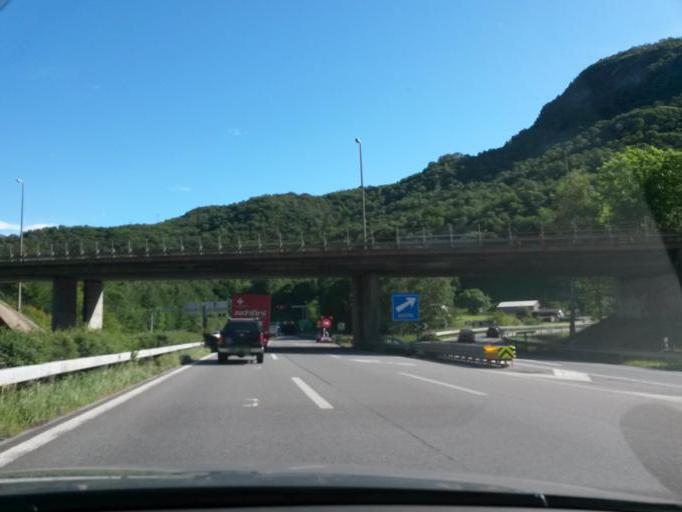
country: CH
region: Ticino
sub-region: Bellinzona District
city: Cadenazzo
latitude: 46.1302
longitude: 8.9186
